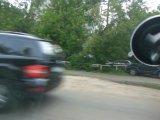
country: RU
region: Moskovskaya
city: Zhukovskiy
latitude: 55.5965
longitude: 38.1365
